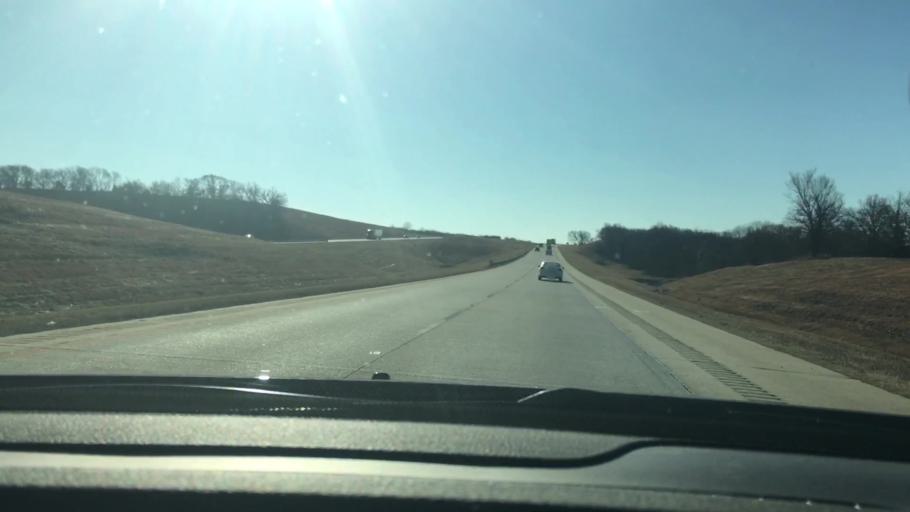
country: US
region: Oklahoma
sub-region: Love County
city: Marietta
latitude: 33.9879
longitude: -97.1384
